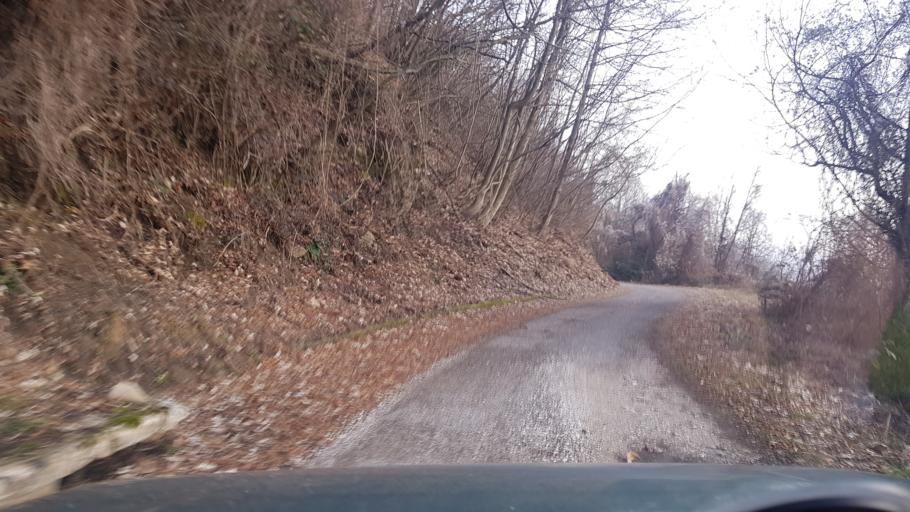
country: IT
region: Friuli Venezia Giulia
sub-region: Provincia di Udine
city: Torreano
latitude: 46.1621
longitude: 13.4426
